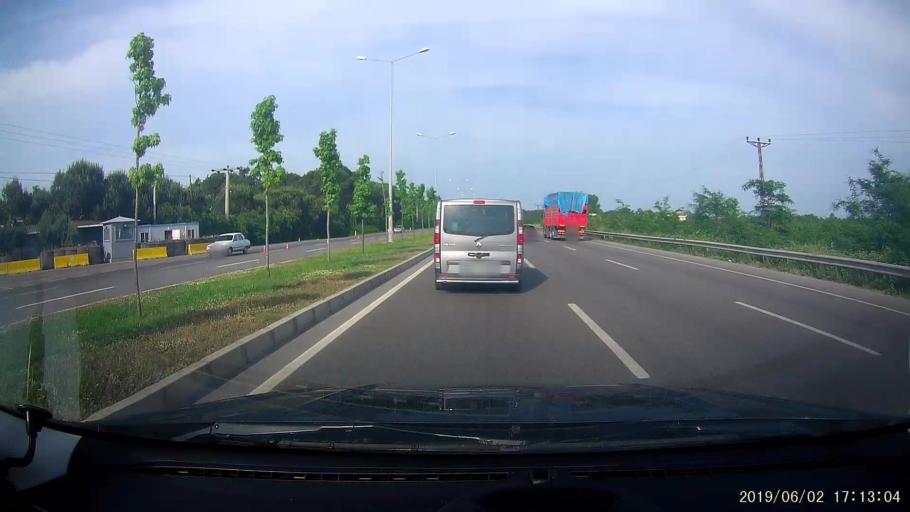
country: TR
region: Samsun
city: Tekkekoy
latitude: 41.2305
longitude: 36.5006
